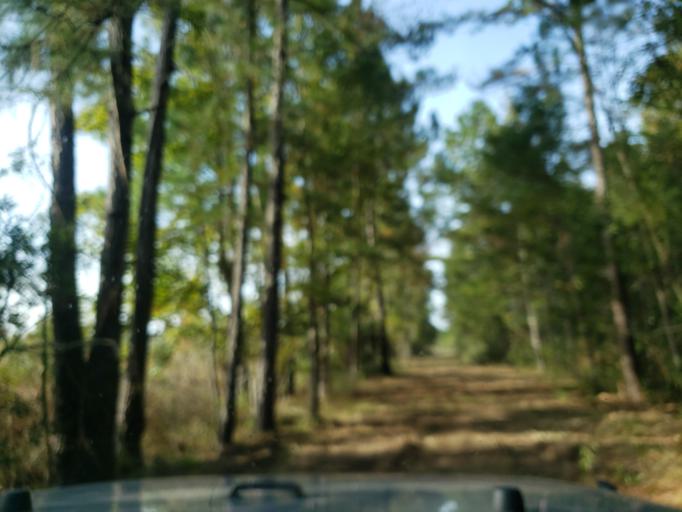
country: US
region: Georgia
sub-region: Chatham County
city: Georgetown
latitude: 32.0448
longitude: -81.2415
